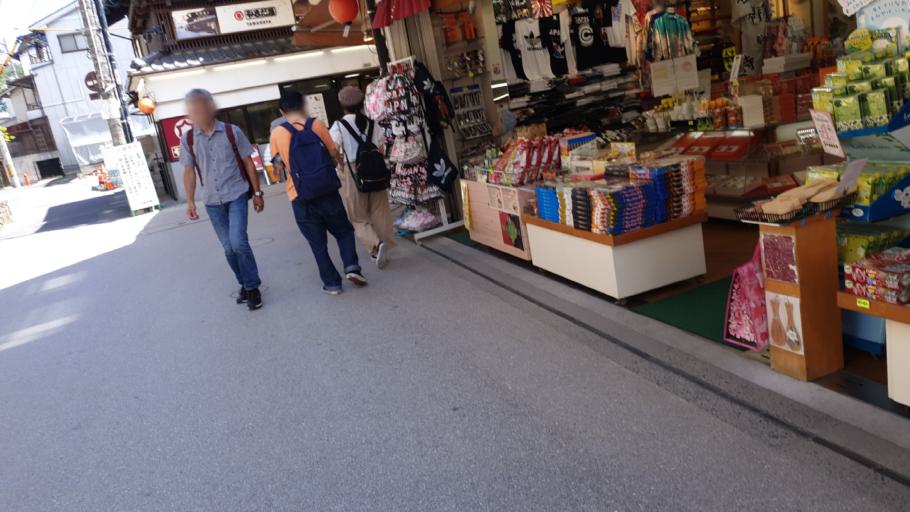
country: JP
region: Hiroshima
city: Miyajima
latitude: 34.2999
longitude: 132.3217
